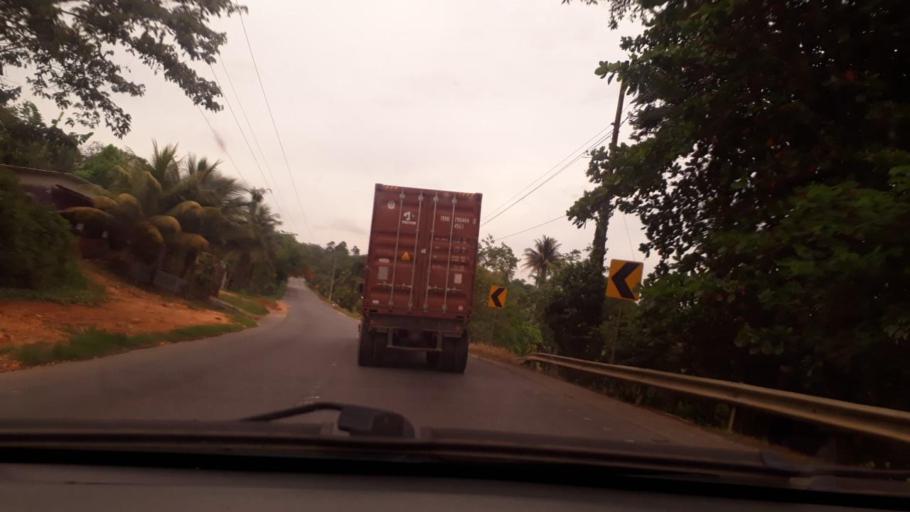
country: GT
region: Izabal
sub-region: Municipio de Puerto Barrios
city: Puerto Barrios
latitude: 15.6002
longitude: -88.5700
